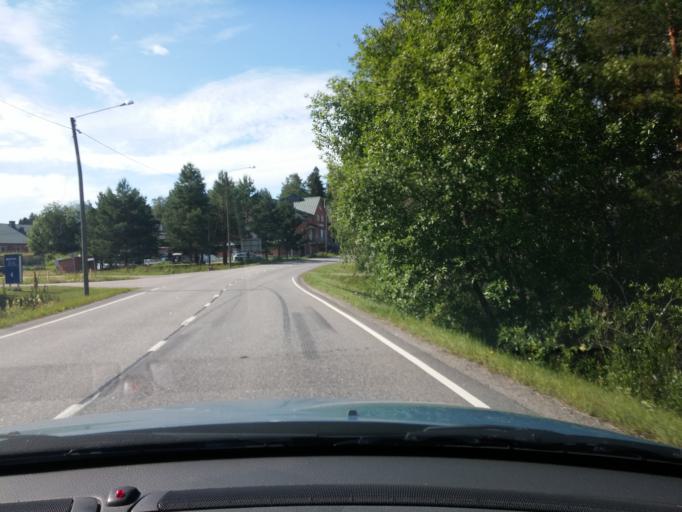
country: FI
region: Uusimaa
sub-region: Porvoo
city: Askola
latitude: 60.4962
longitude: 25.5526
